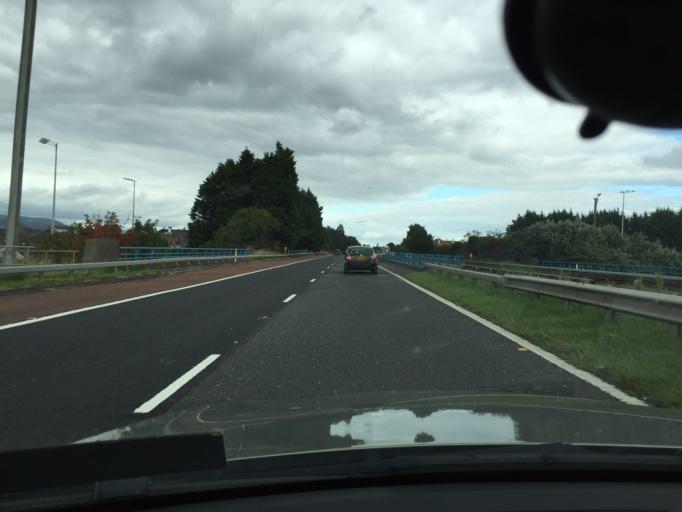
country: GB
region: Northern Ireland
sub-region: Lisburn District
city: Lisburn
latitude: 54.5051
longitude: -6.0296
